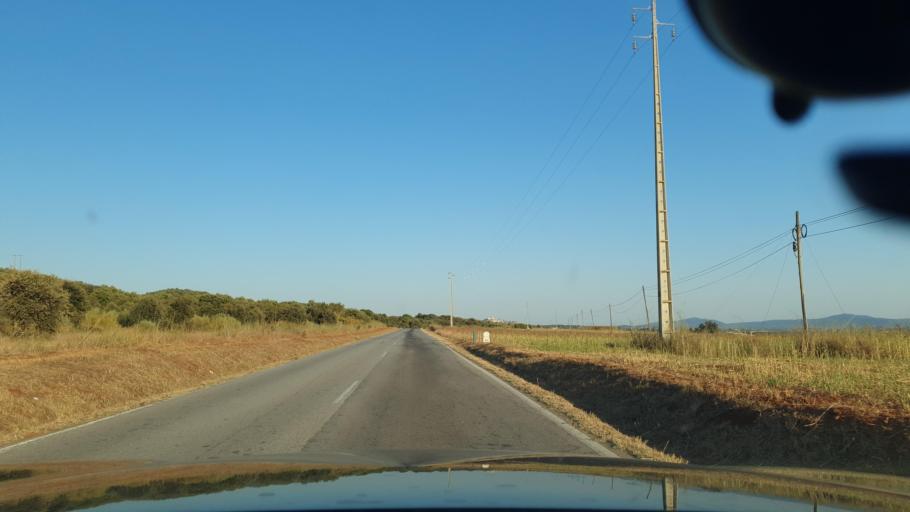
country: PT
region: Evora
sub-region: Estremoz
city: Estremoz
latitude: 38.8867
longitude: -7.6499
